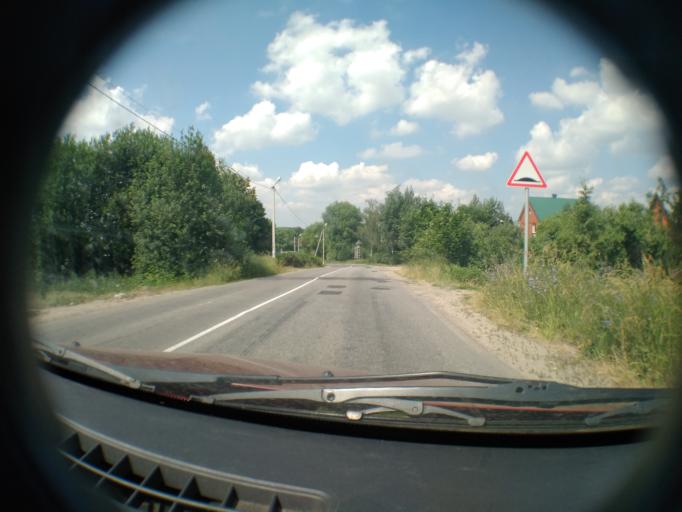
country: RU
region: Moskovskaya
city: Yakovlevskoye
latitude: 55.4253
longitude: 37.9546
